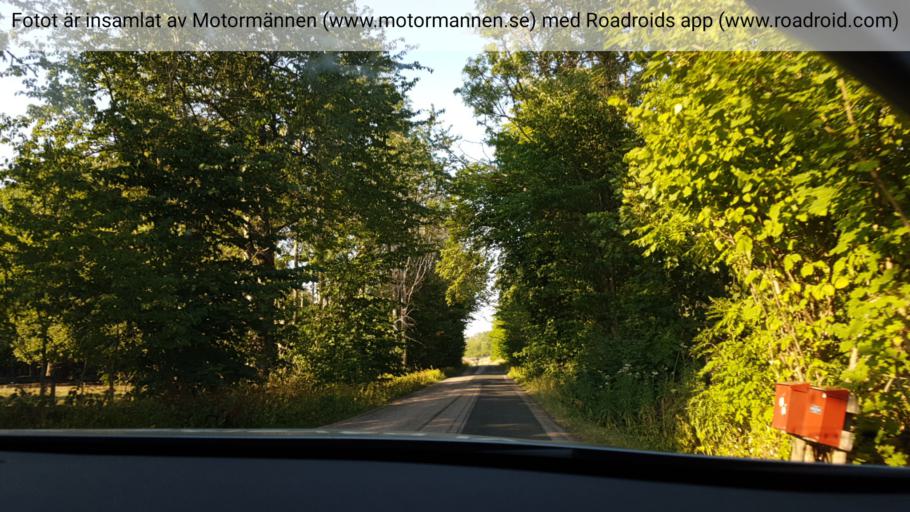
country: SE
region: Vaestra Goetaland
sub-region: Skovde Kommun
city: Skoevde
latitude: 58.4580
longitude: 13.7357
